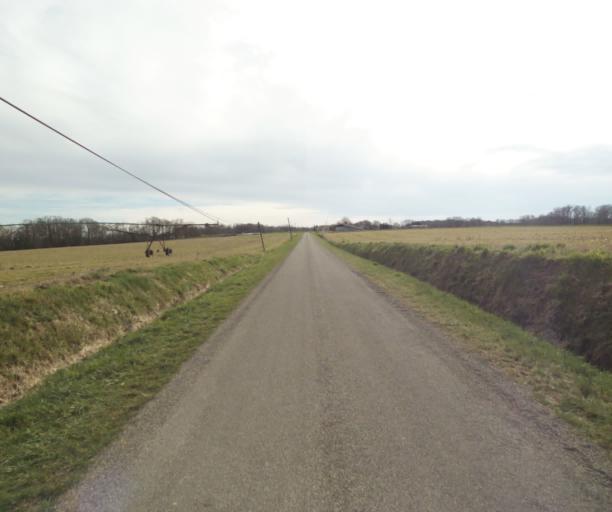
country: FR
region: Aquitaine
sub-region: Departement des Landes
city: Gabarret
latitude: 43.9354
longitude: 0.0453
